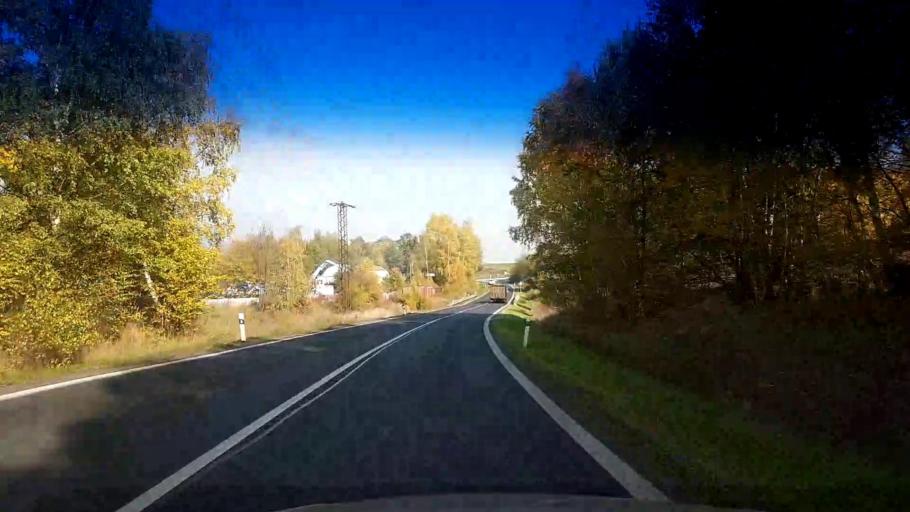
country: CZ
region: Karlovarsky
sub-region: Okres Cheb
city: Cheb
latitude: 50.0734
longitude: 12.3906
